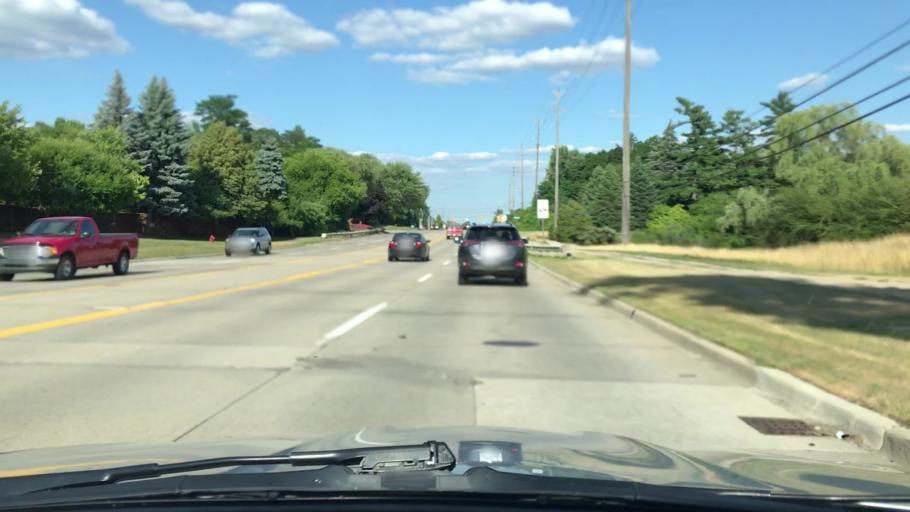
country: US
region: Michigan
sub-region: Wayne County
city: Northville
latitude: 42.4386
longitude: -83.4431
